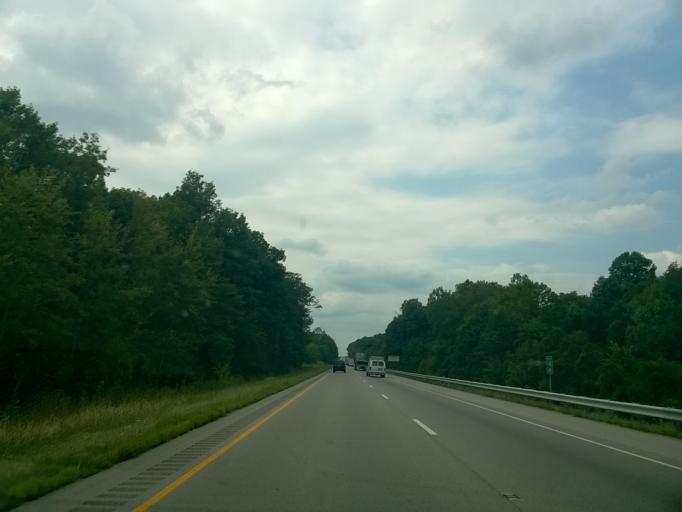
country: US
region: Indiana
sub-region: Putnam County
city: Cloverdale
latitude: 39.5406
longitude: -86.7539
